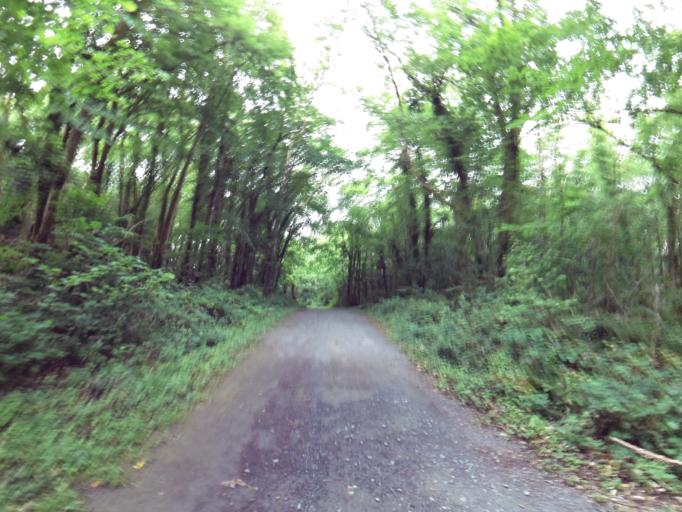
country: IE
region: Connaught
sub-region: County Galway
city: Gort
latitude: 53.0790
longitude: -8.8635
